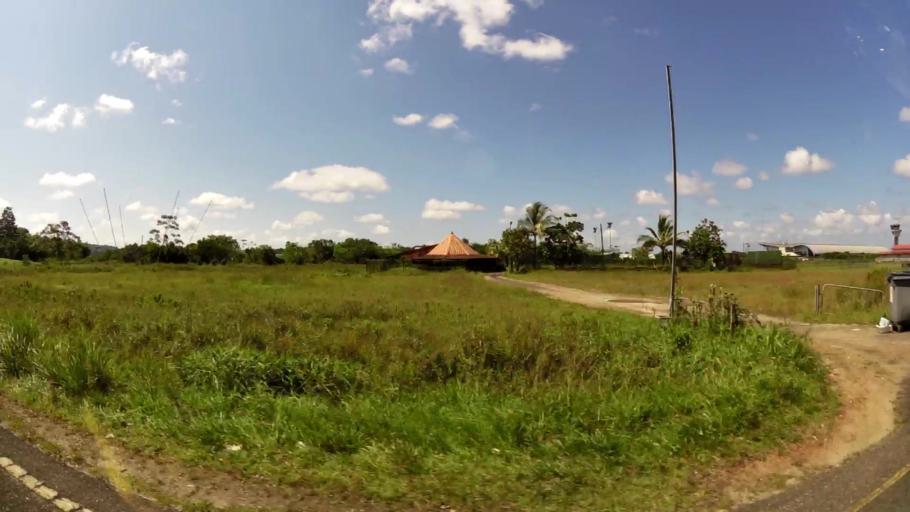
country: GF
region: Guyane
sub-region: Guyane
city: Matoury
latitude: 4.8260
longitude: -52.3621
